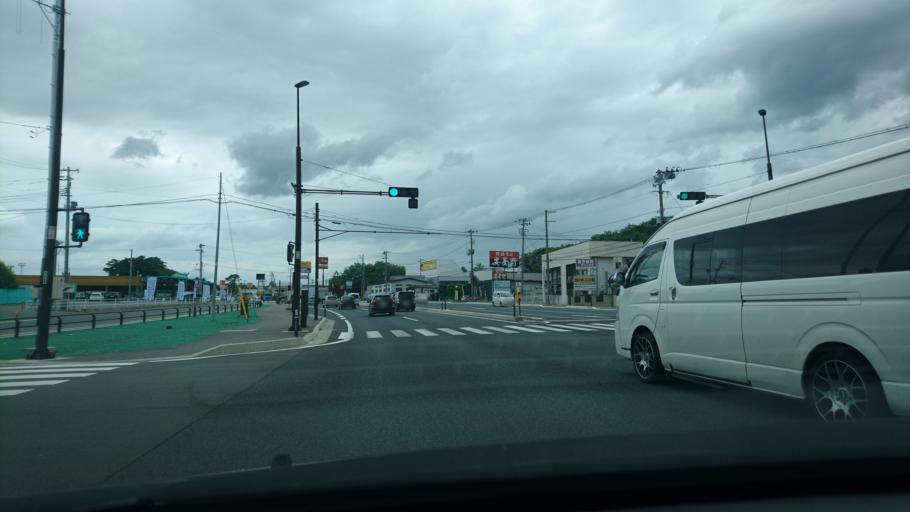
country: JP
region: Iwate
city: Morioka-shi
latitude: 39.7696
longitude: 141.1307
